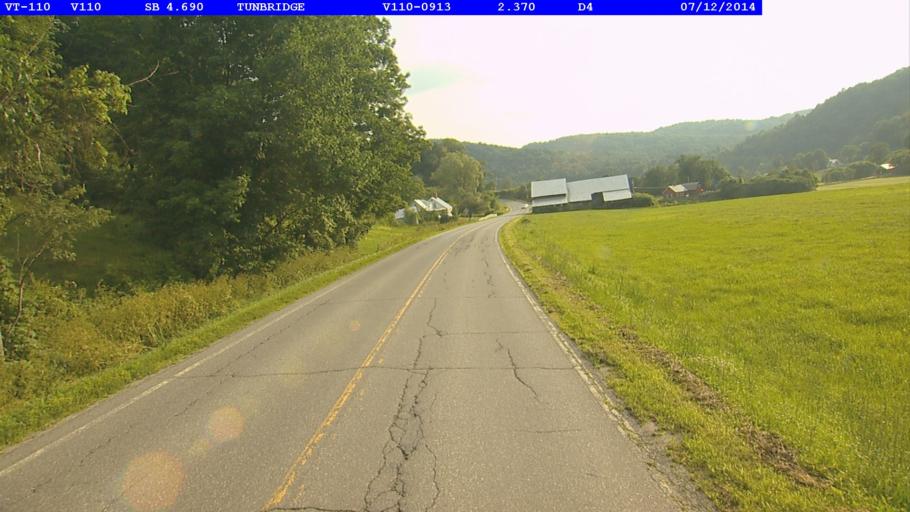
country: US
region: Vermont
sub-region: Orange County
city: Chelsea
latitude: 43.8832
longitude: -72.4983
